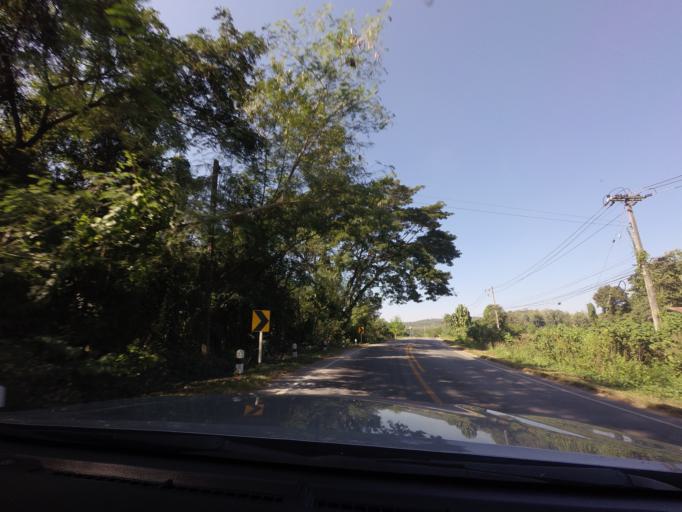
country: TH
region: Sukhothai
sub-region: Amphoe Si Satchanalai
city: Si Satchanalai
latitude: 17.6266
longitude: 99.7012
